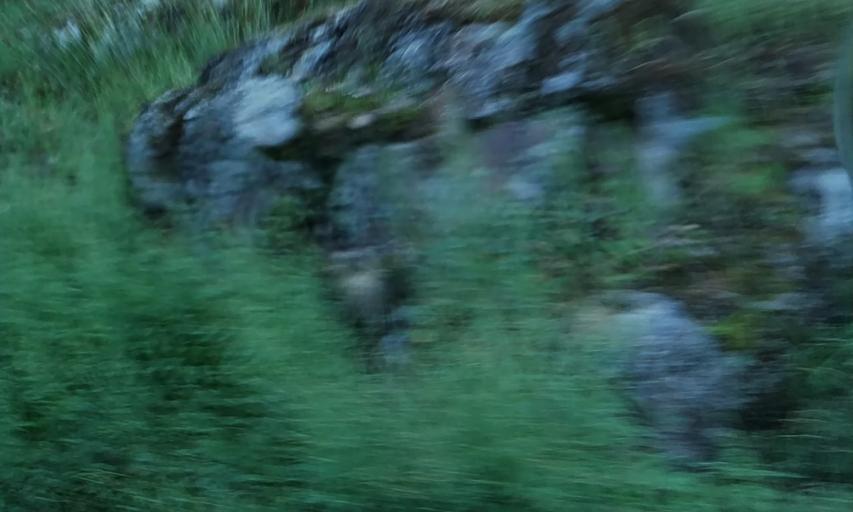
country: PT
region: Portalegre
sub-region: Marvao
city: Marvao
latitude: 39.3677
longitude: -7.3993
